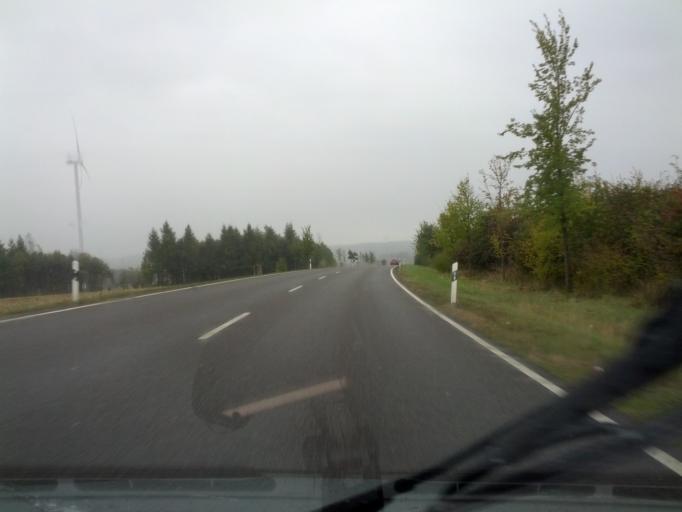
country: DE
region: Saxony
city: Hartenstein
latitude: 50.6845
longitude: 12.7032
